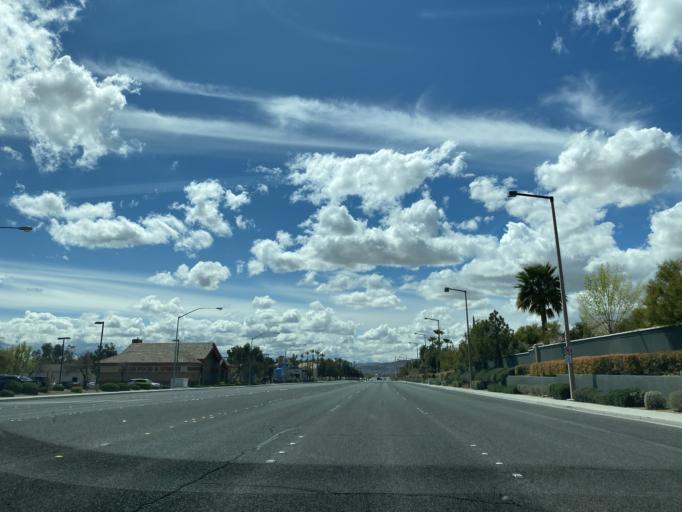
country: US
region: Nevada
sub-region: Clark County
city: Summerlin South
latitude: 36.1284
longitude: -115.3152
